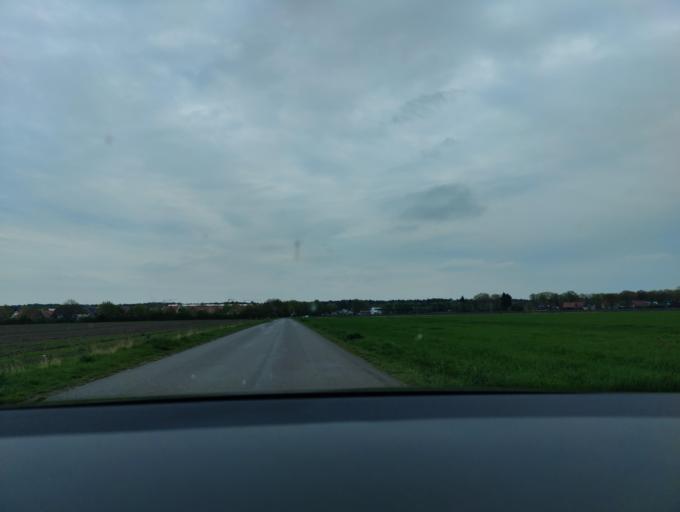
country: DE
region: Lower Saxony
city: Lingen
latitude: 52.4971
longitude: 7.3187
